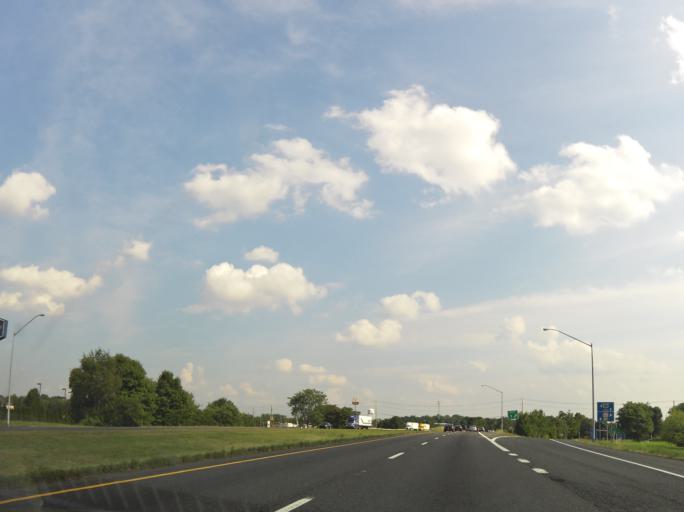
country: US
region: Maryland
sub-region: Washington County
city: Maugansville
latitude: 39.6921
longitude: -77.7338
